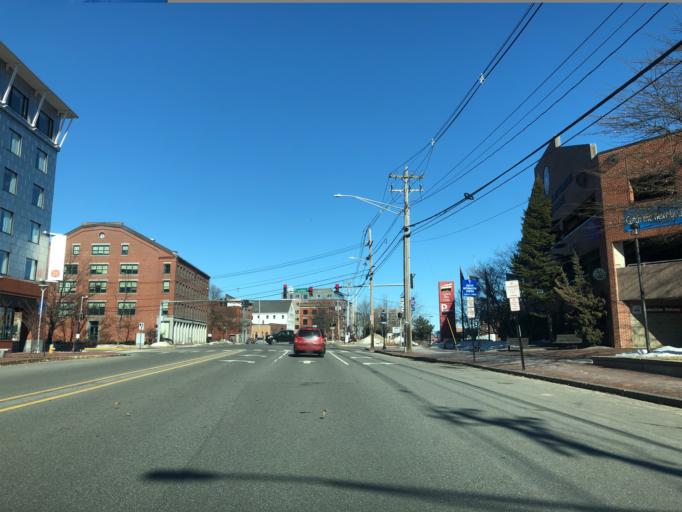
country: US
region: Maine
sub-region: Cumberland County
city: Portland
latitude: 43.6575
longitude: -70.2502
